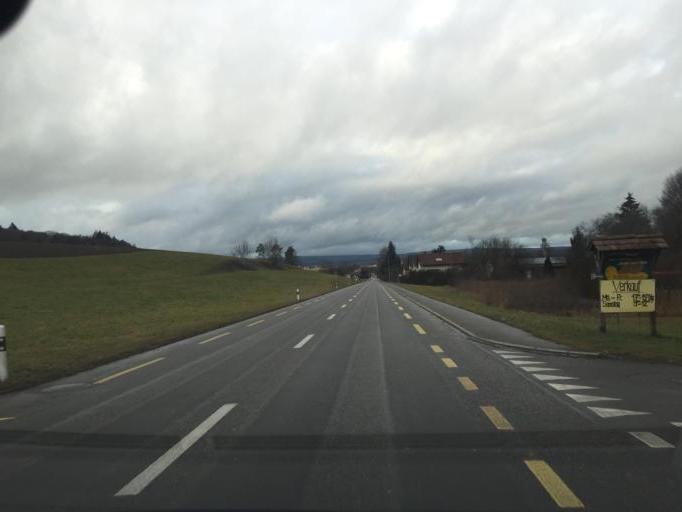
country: DE
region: Baden-Wuerttemberg
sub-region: Freiburg Region
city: Busingen
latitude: 47.6717
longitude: 8.6946
